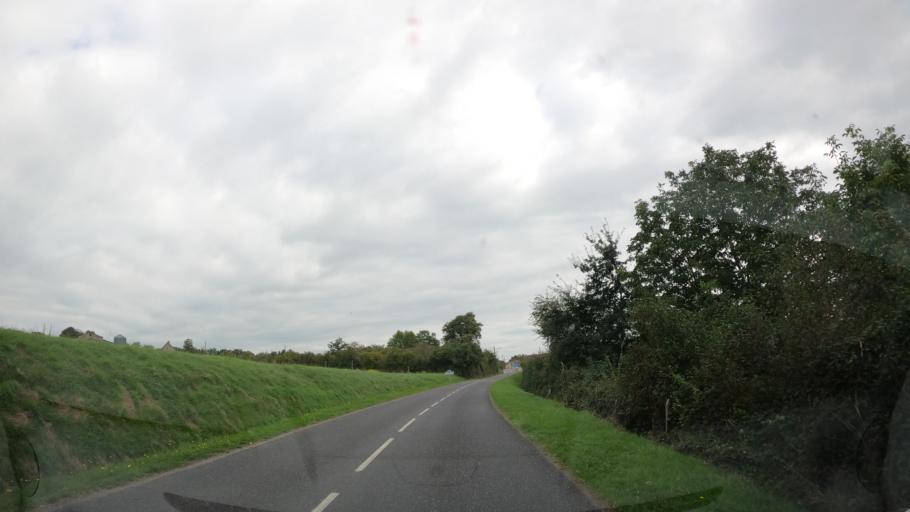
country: FR
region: Auvergne
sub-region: Departement de l'Allier
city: Lapalisse
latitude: 46.3275
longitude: 3.6248
